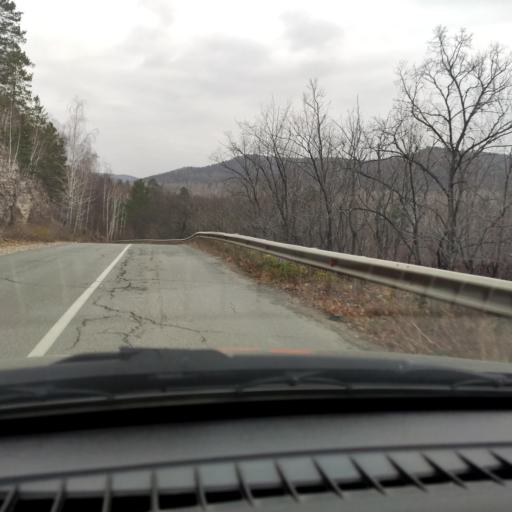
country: RU
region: Samara
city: Povolzhskiy
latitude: 53.4346
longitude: 49.6706
